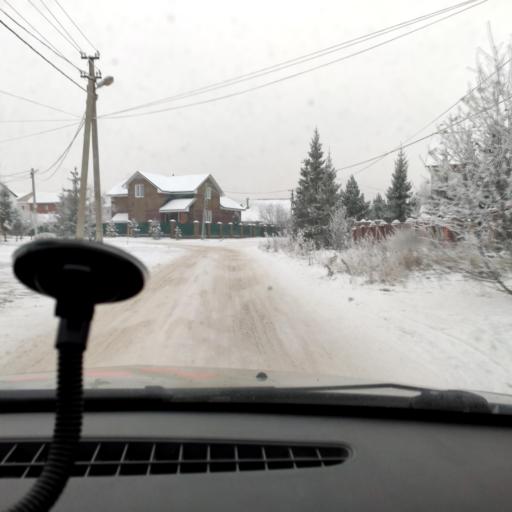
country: RU
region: Bashkortostan
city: Ufa
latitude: 54.6014
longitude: 55.9320
